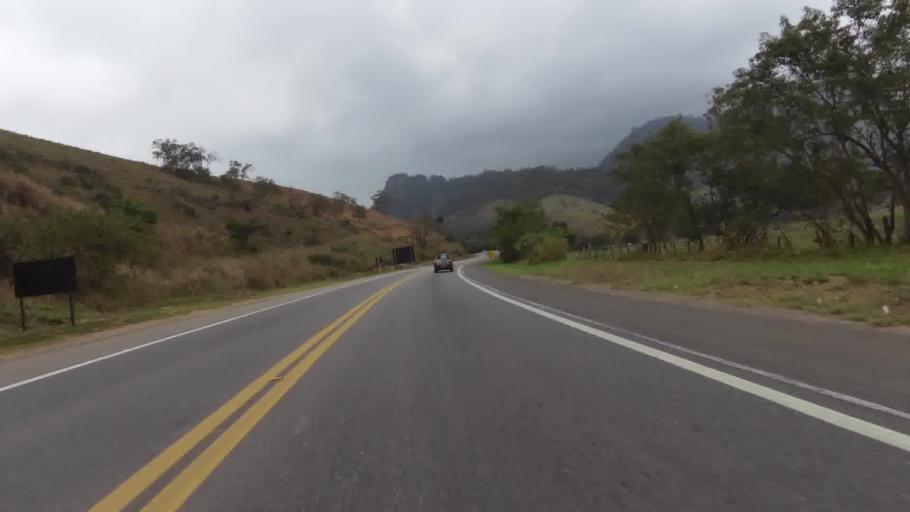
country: BR
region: Espirito Santo
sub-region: Rio Novo Do Sul
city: Rio Novo do Sul
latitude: -20.8815
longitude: -40.9733
